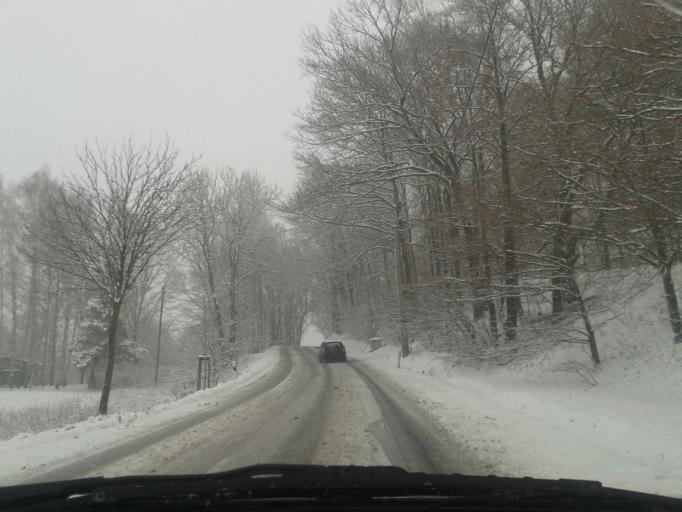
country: DE
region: Saxony
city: Durrrohrsdorf
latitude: 51.0453
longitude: 13.9349
